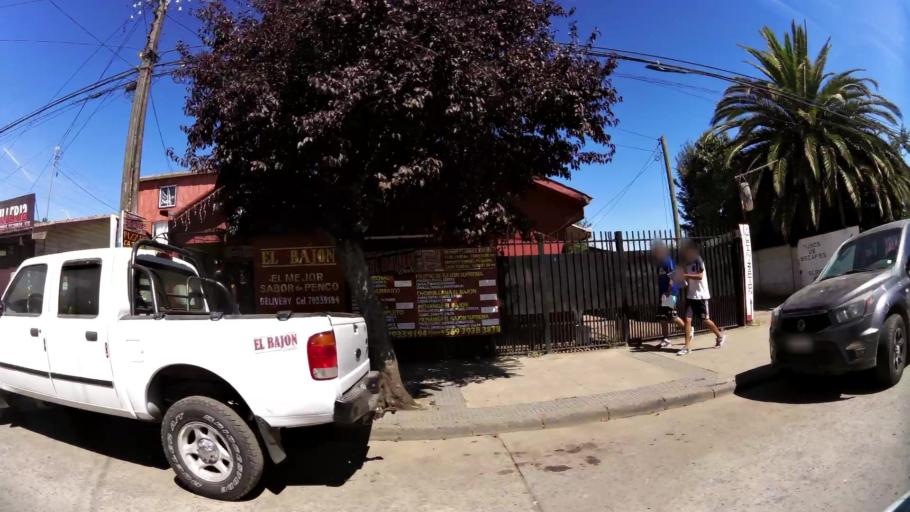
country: CL
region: Biobio
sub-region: Provincia de Concepcion
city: Penco
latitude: -36.7373
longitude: -72.9910
